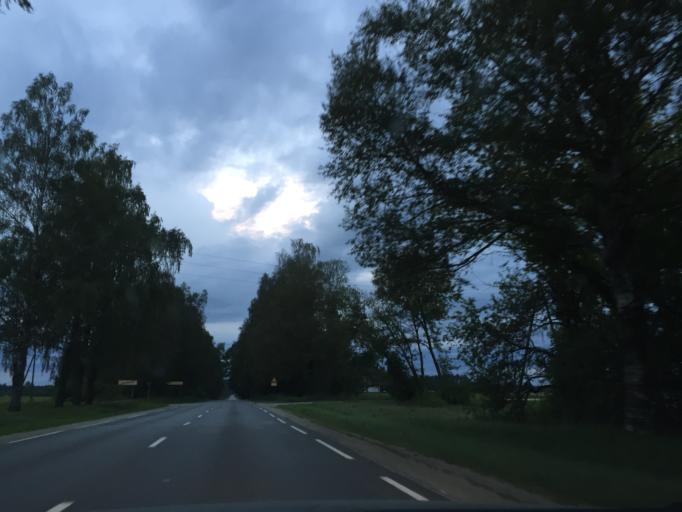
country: LV
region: Vecumnieki
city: Vecumnieki
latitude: 56.6150
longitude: 24.5052
